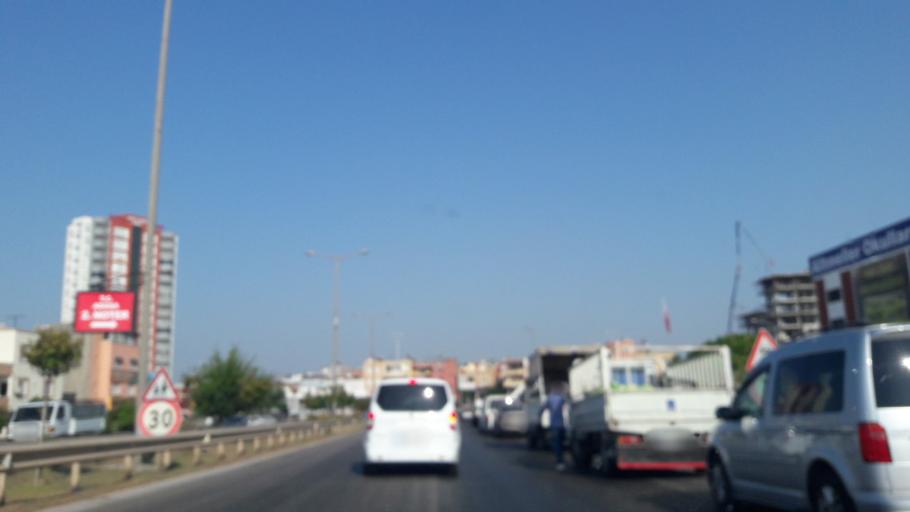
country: TR
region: Adana
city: Yuregir
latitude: 37.0241
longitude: 35.4004
